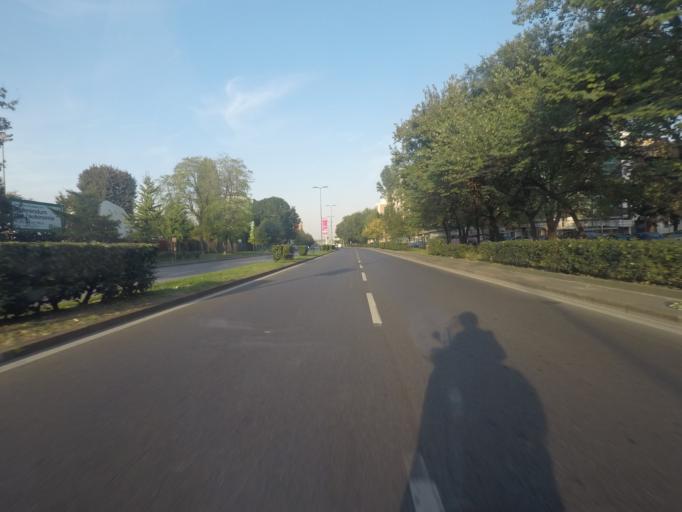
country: IT
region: Lombardy
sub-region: Citta metropolitana di Milano
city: Sesto San Giovanni
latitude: 45.4937
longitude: 9.2328
